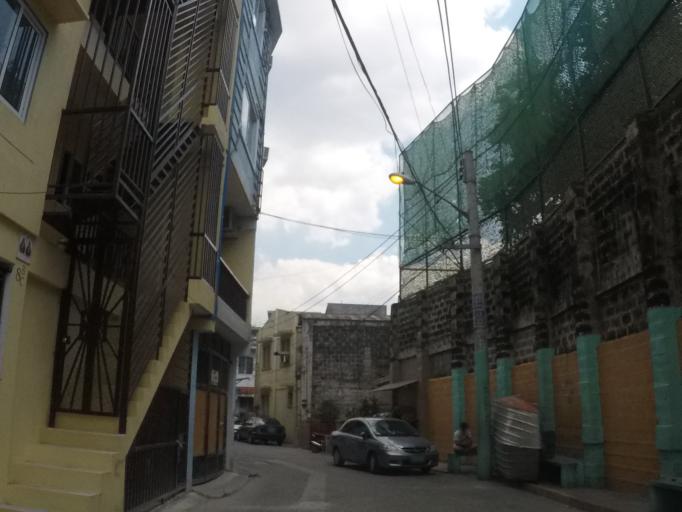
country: PH
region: Metro Manila
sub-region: San Juan
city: San Juan
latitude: 14.6043
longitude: 121.0215
